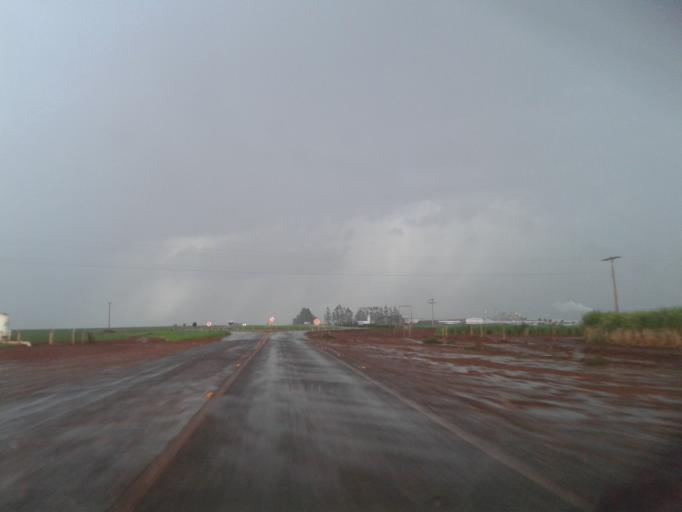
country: BR
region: Goias
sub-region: Quirinopolis
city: Quirinopolis
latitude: -18.5593
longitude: -50.4395
